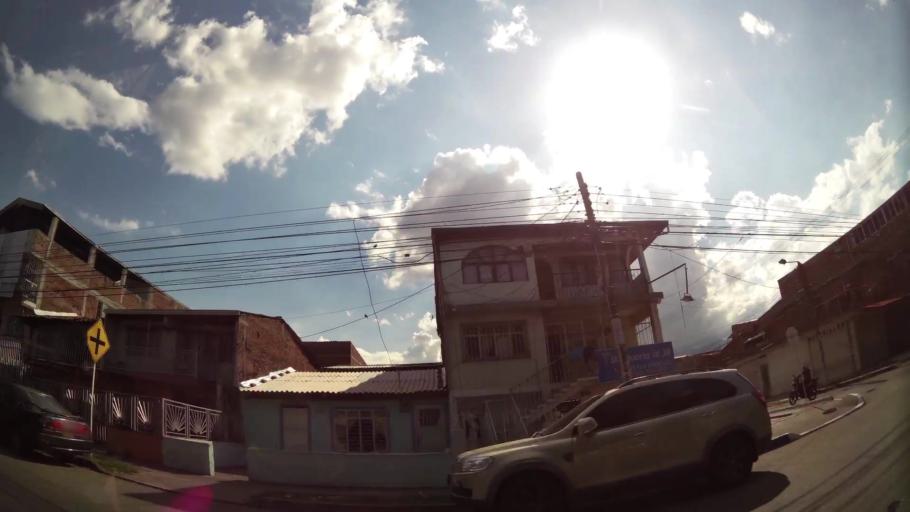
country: CO
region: Valle del Cauca
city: Cali
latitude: 3.4177
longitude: -76.5065
